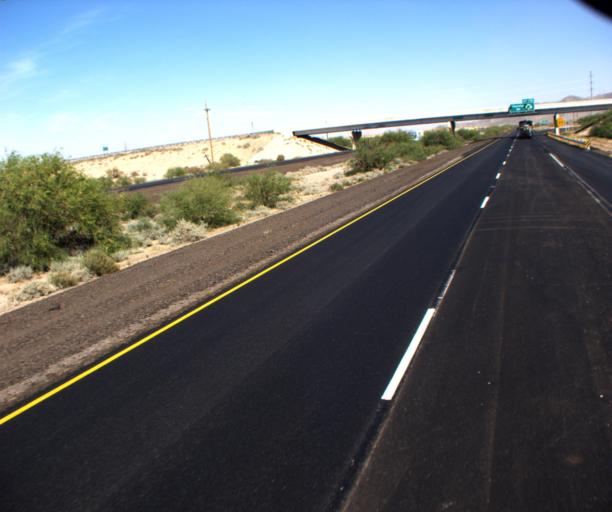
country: US
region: Arizona
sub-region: Pinal County
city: Casa Grande
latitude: 32.8279
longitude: -111.7760
